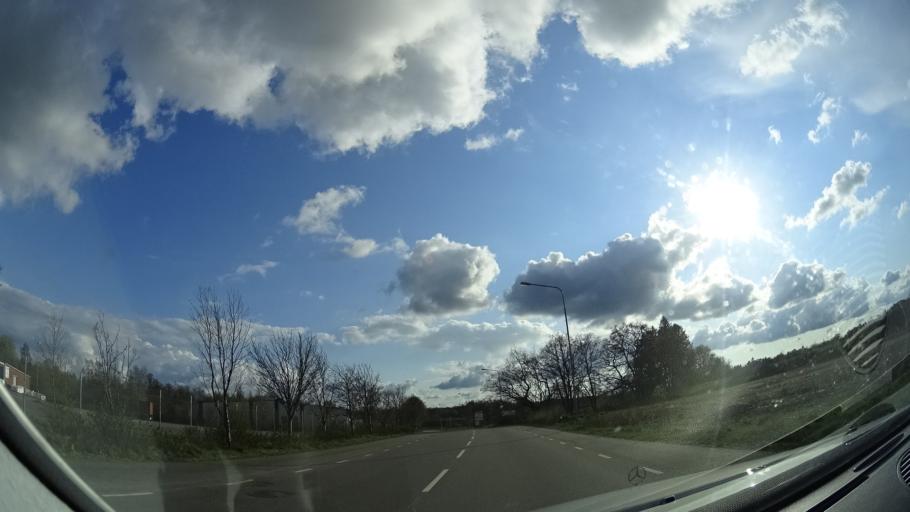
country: SE
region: Skane
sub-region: Perstorps Kommun
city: Perstorp
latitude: 56.1427
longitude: 13.3799
